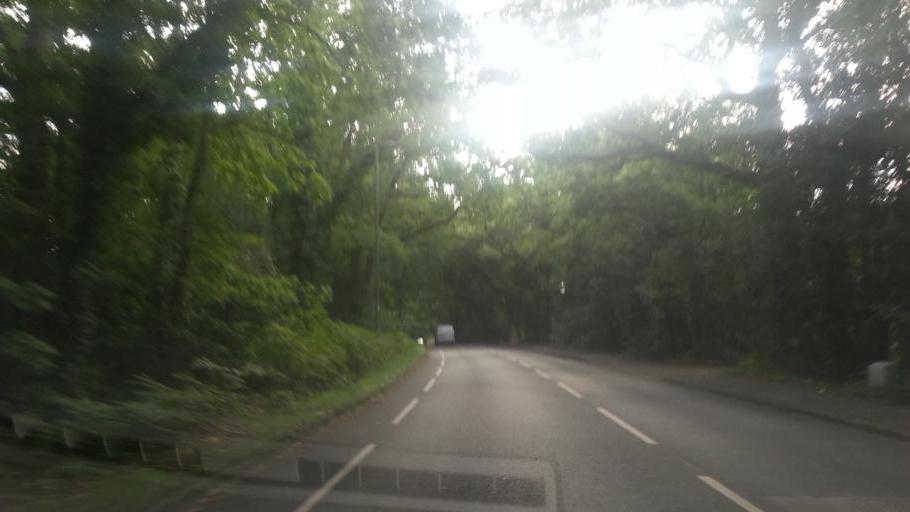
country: GB
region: England
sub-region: Surrey
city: West Byfleet
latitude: 51.3220
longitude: -0.5265
